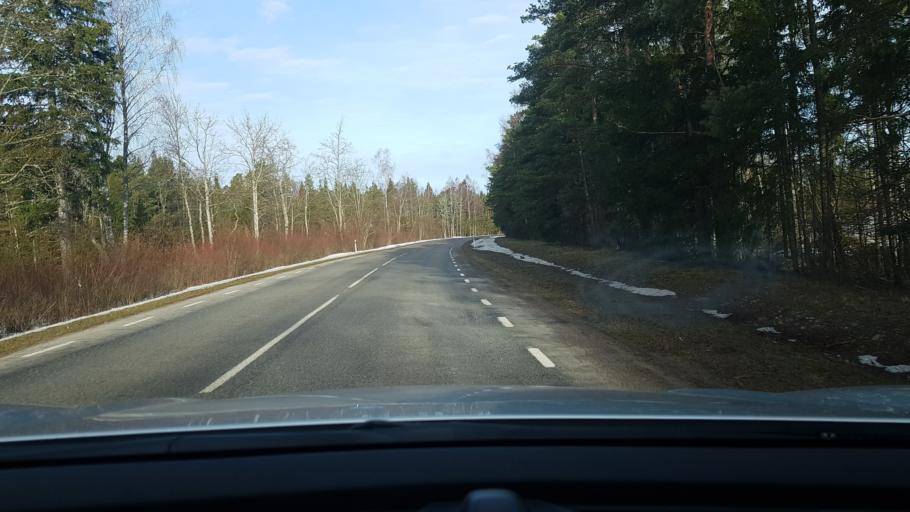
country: EE
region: Saare
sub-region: Kuressaare linn
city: Kuressaare
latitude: 58.4636
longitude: 22.7023
